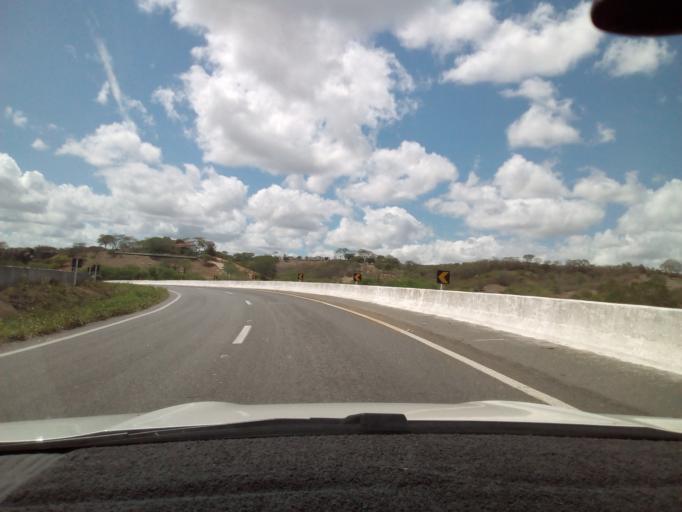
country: BR
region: Paraiba
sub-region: Massaranduba
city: Massaranduba
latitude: -7.2757
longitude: -35.7831
